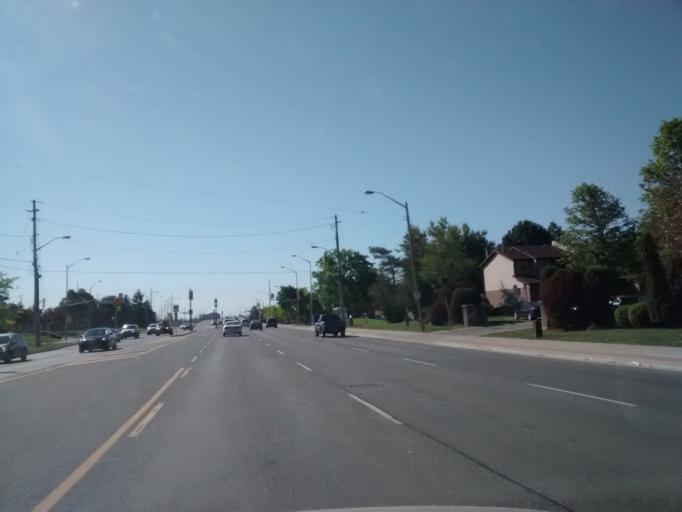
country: CA
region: Ontario
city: Burlington
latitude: 43.3577
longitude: -79.8118
